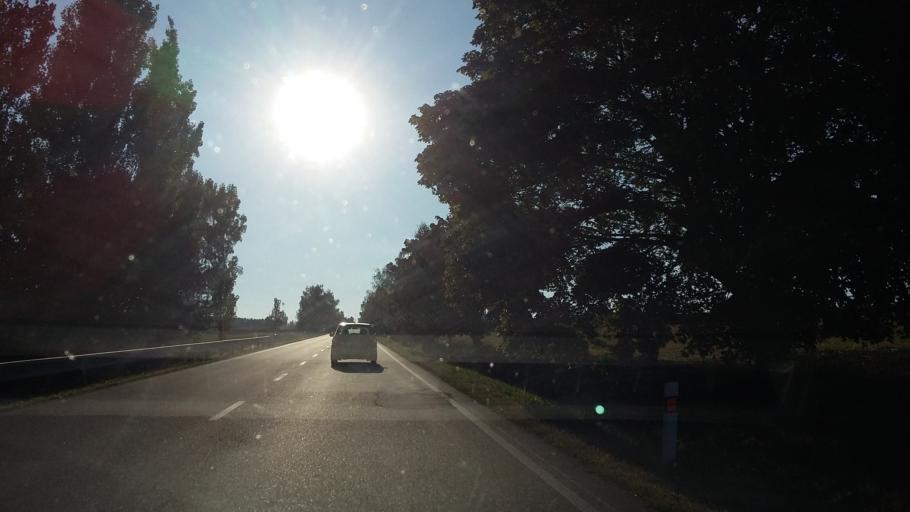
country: CZ
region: Vysocina
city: Merin
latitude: 49.4006
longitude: 15.8419
